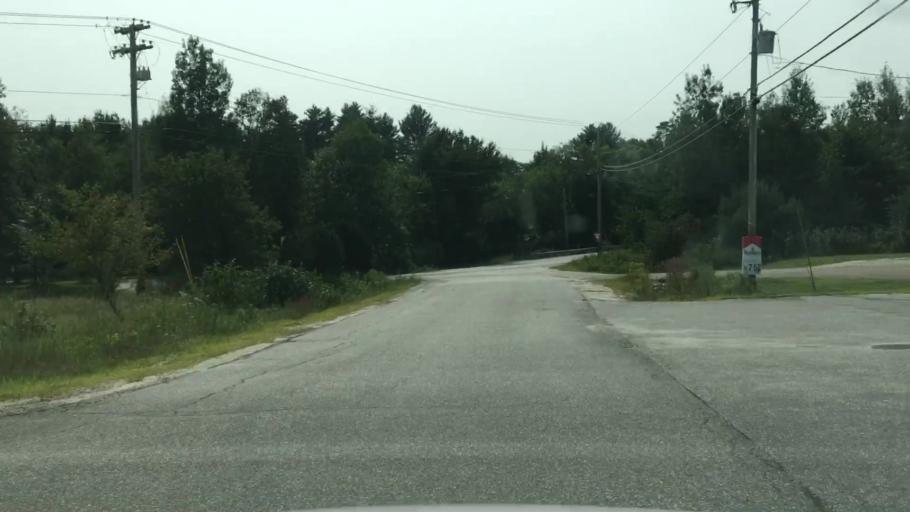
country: US
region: Maine
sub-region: Oxford County
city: Buckfield
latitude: 44.2857
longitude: -70.3508
